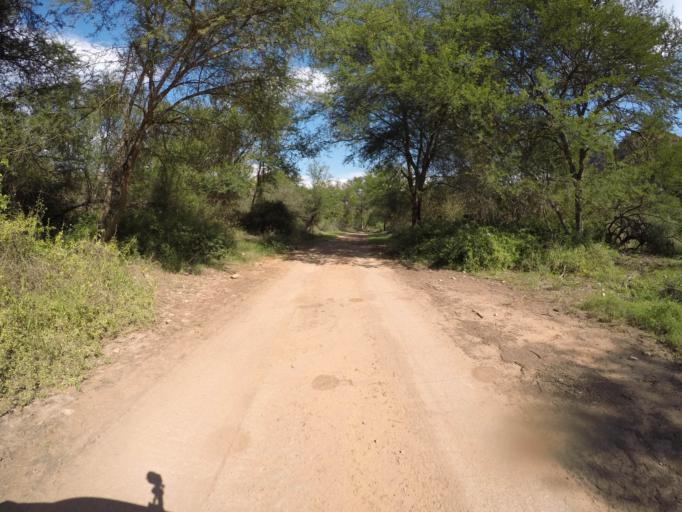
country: ZA
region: Eastern Cape
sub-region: Cacadu District Municipality
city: Kareedouw
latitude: -33.6644
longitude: 24.3886
